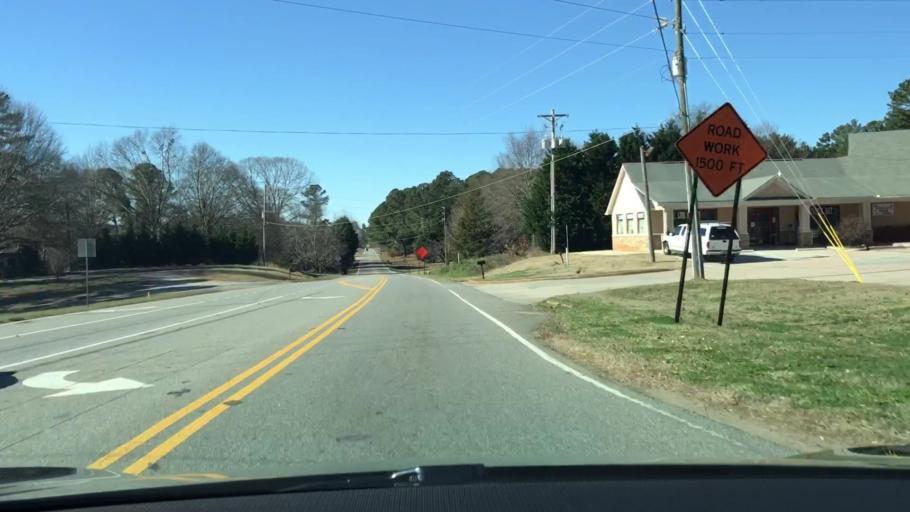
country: US
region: Georgia
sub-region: Forsyth County
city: Cumming
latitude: 34.1802
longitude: -84.0887
